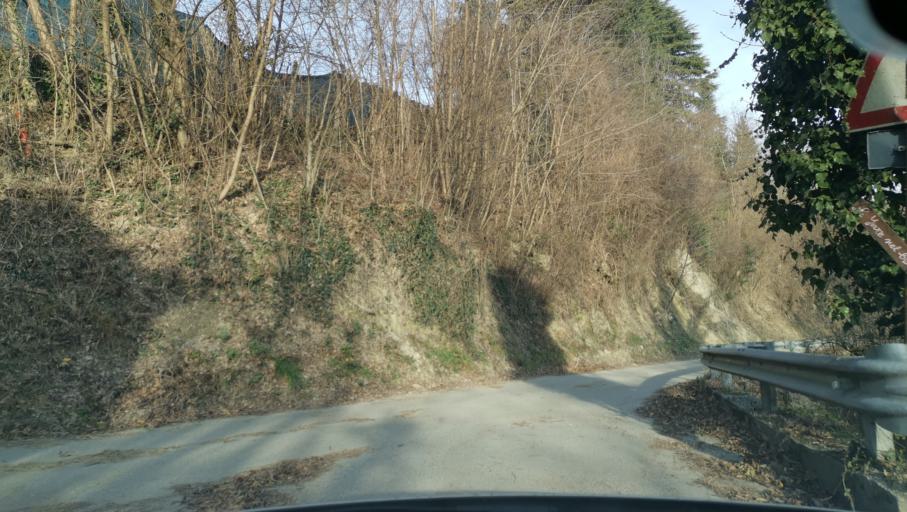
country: IT
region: Piedmont
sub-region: Provincia di Torino
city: Gassino Torinese
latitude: 45.1180
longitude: 7.8273
